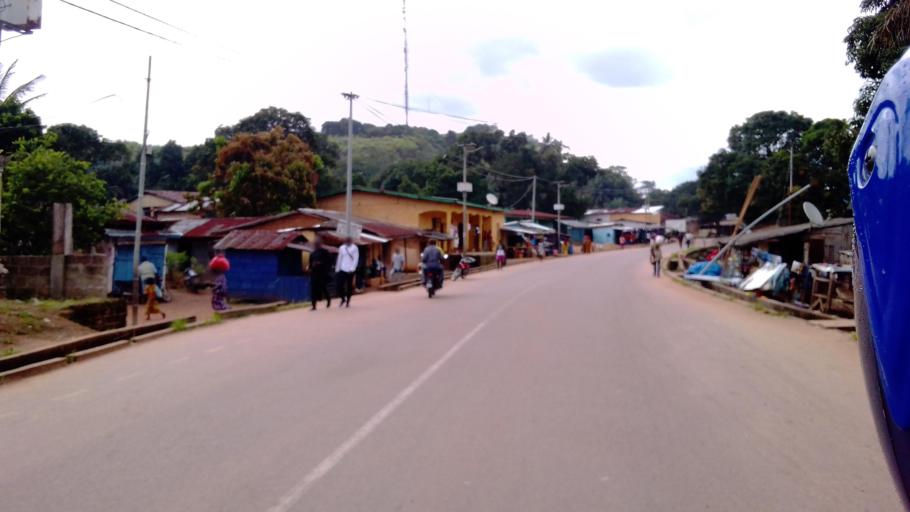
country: SL
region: Eastern Province
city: Koidu
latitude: 8.6485
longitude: -10.9752
